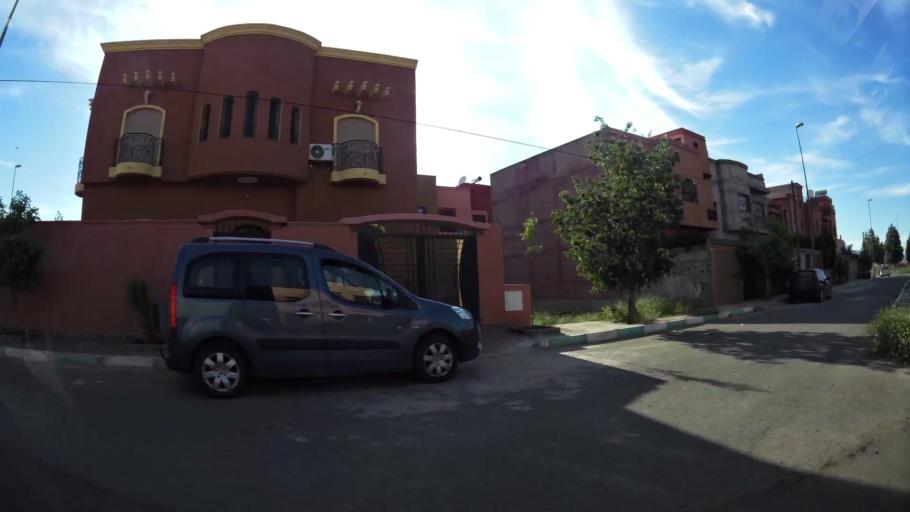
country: MA
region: Marrakech-Tensift-Al Haouz
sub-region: Marrakech
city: Marrakesh
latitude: 31.6906
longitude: -8.0631
